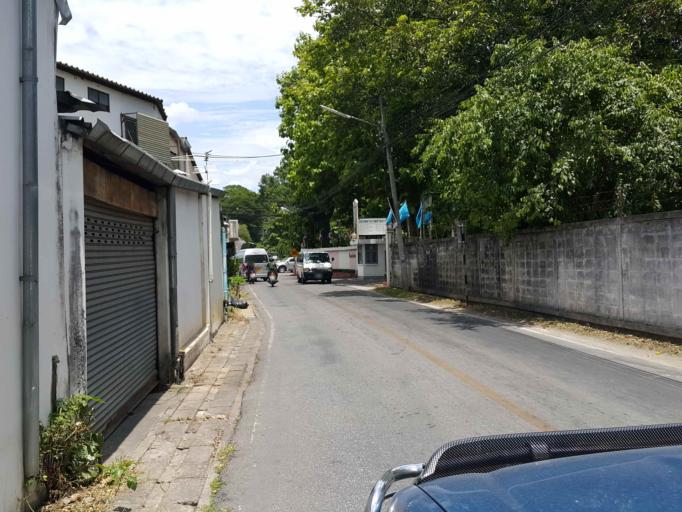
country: TH
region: Chiang Mai
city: Chiang Mai
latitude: 18.7785
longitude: 99.0162
